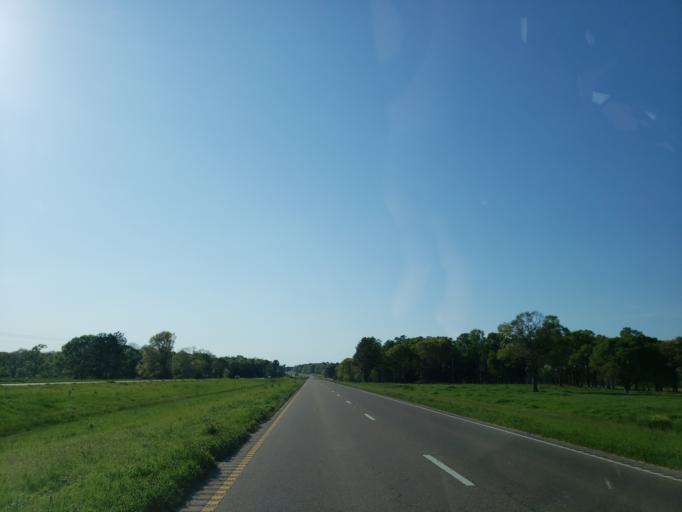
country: US
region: Mississippi
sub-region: Jones County
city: Ellisville
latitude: 31.6791
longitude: -89.3042
